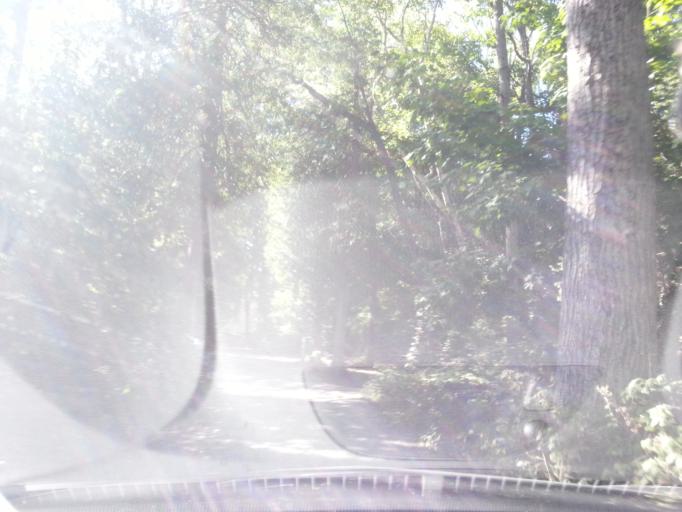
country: CA
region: Ontario
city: Prince Edward
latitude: 43.9042
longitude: -77.2314
